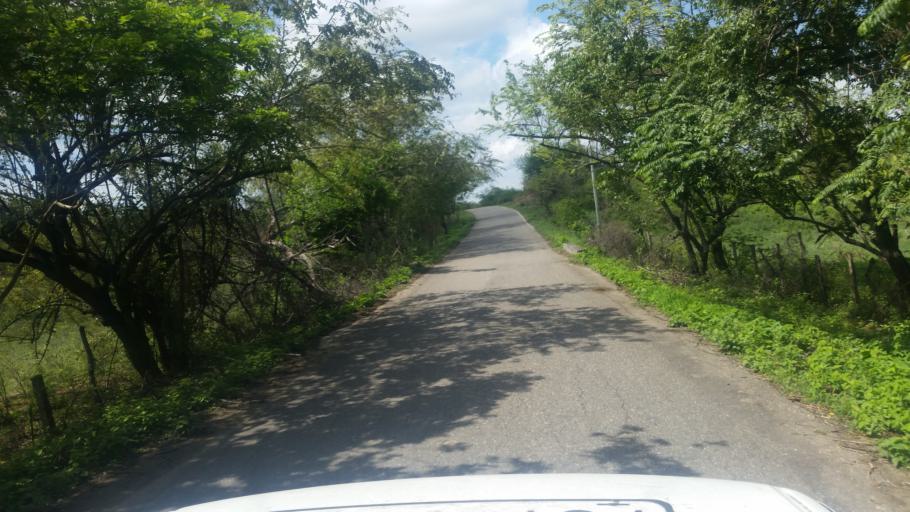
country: CO
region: Huila
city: Villavieja
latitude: 3.1924
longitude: -75.2156
